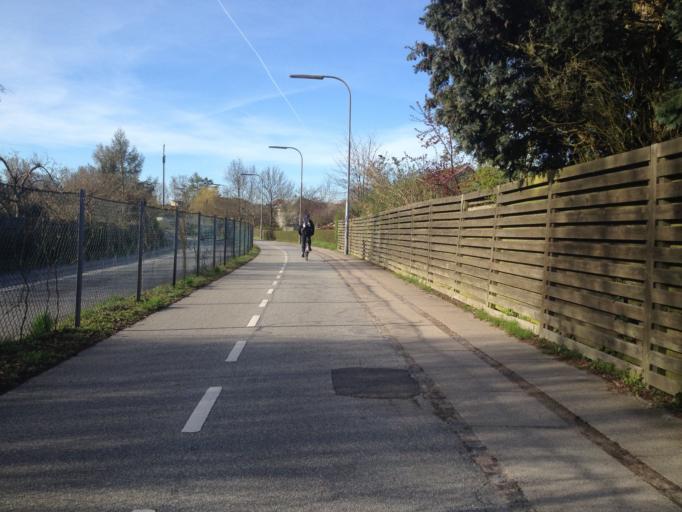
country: DK
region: Capital Region
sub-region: Ballerup Kommune
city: Ballerup
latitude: 55.7504
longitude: 12.3829
